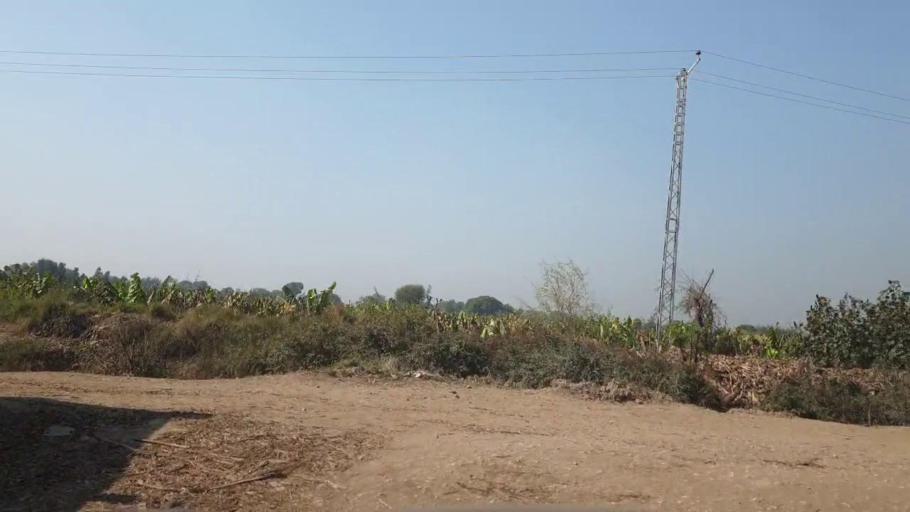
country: PK
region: Sindh
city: Tando Allahyar
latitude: 25.4655
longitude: 68.6934
